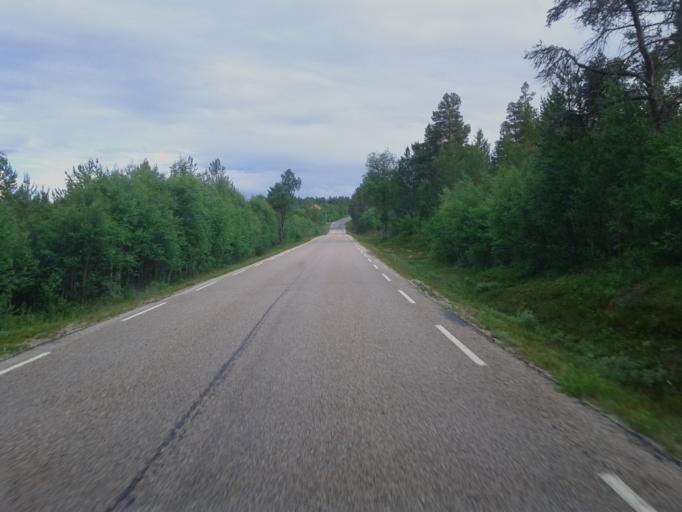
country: NO
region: Hedmark
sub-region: Engerdal
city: Engerdal
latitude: 62.0566
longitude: 11.6845
